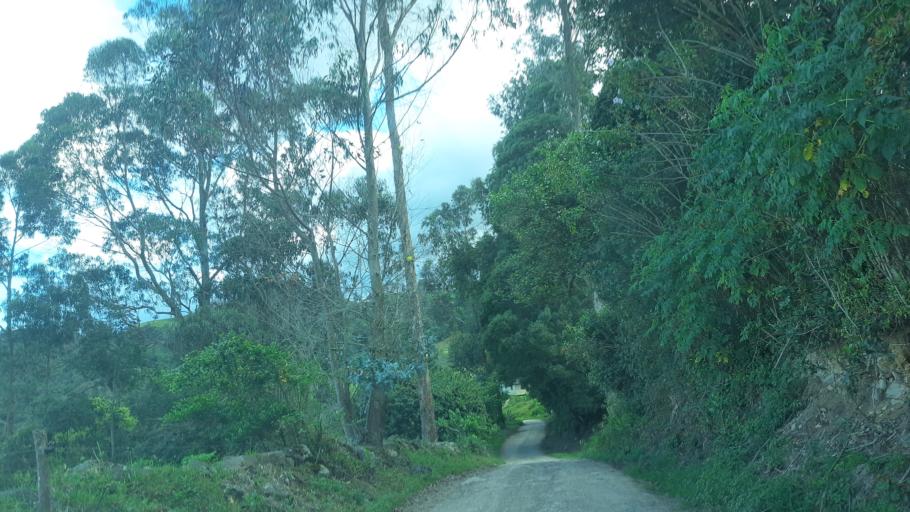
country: CO
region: Cundinamarca
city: Macheta
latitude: 5.0718
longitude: -73.6313
